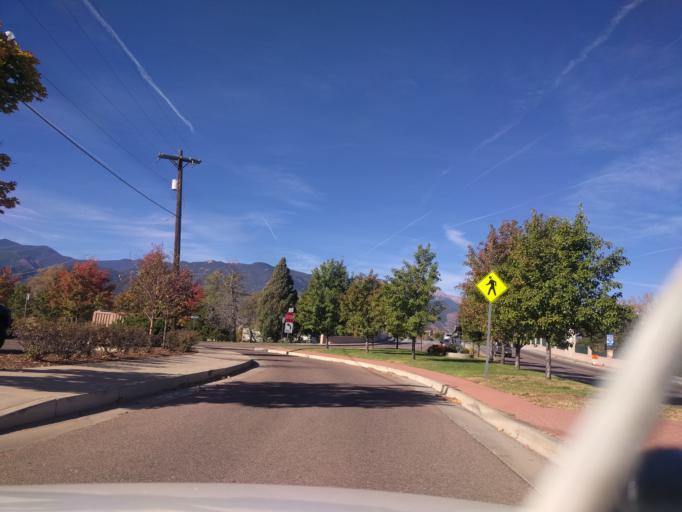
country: US
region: Colorado
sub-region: El Paso County
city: Colorado Springs
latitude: 38.8368
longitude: -104.8270
